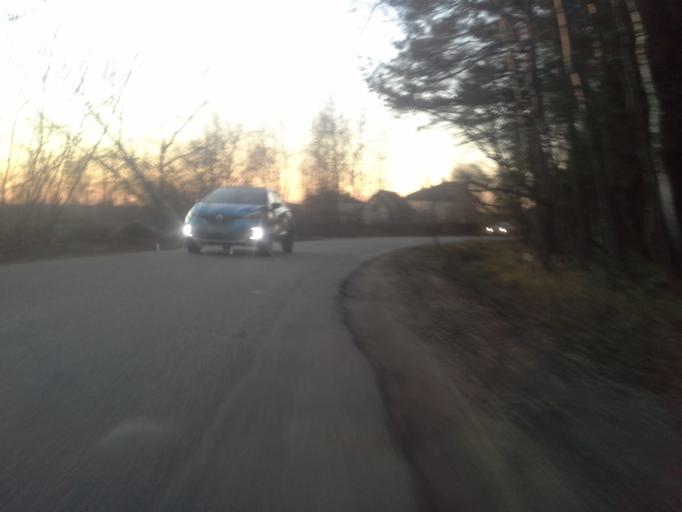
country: RU
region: Moscow
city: Tolstopal'tsevo
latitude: 55.6091
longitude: 37.2373
